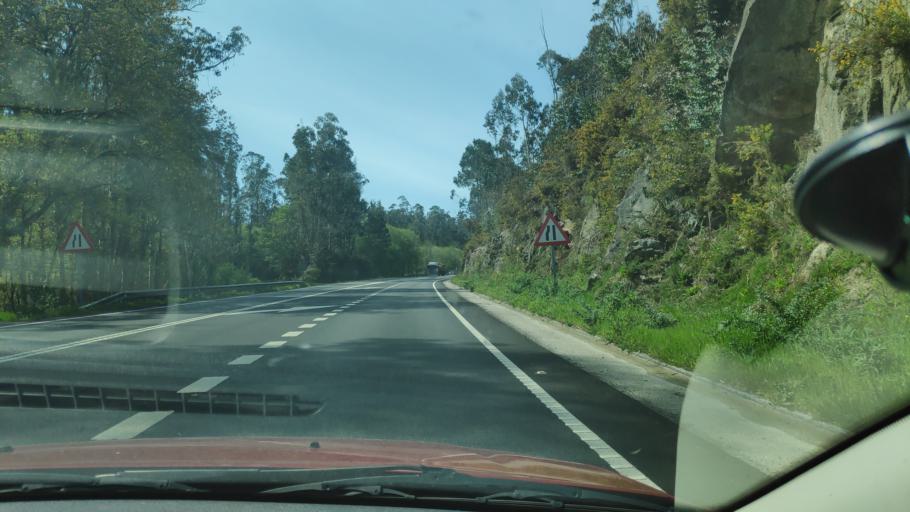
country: ES
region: Galicia
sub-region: Provincia da Coruna
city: Ames
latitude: 42.8763
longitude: -8.6728
